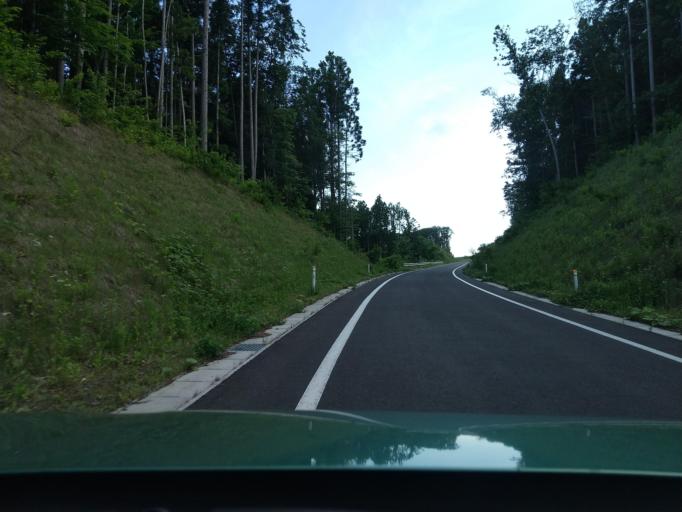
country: JP
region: Iwate
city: Ichinoseki
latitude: 38.9911
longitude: 141.2186
